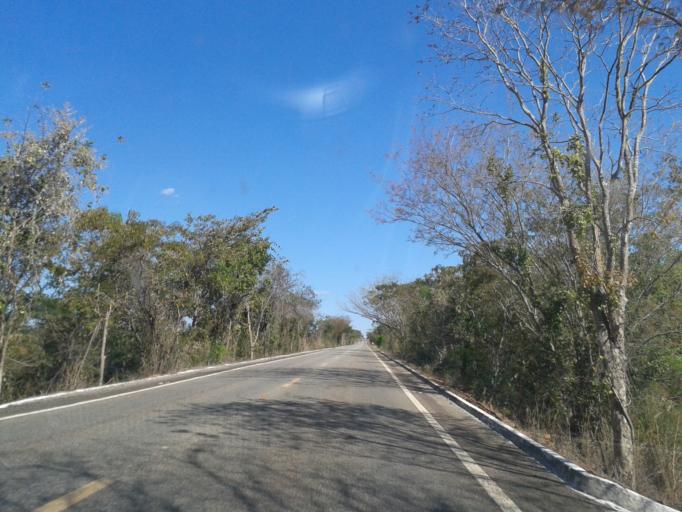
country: BR
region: Goias
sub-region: Sao Miguel Do Araguaia
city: Sao Miguel do Araguaia
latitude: -13.6873
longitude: -50.3309
